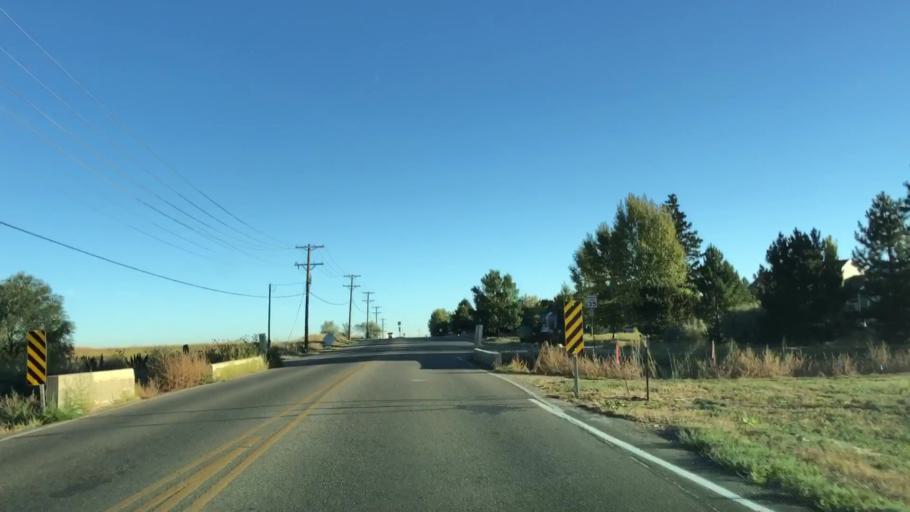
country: US
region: Colorado
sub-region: Larimer County
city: Loveland
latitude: 40.4097
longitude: -105.0210
